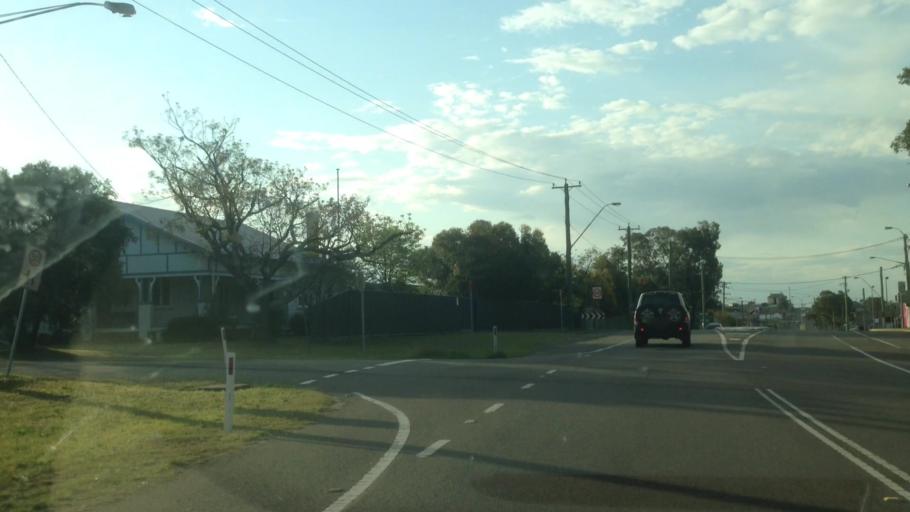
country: AU
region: New South Wales
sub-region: Cessnock
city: Kurri Kurri
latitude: -32.8269
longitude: 151.4877
